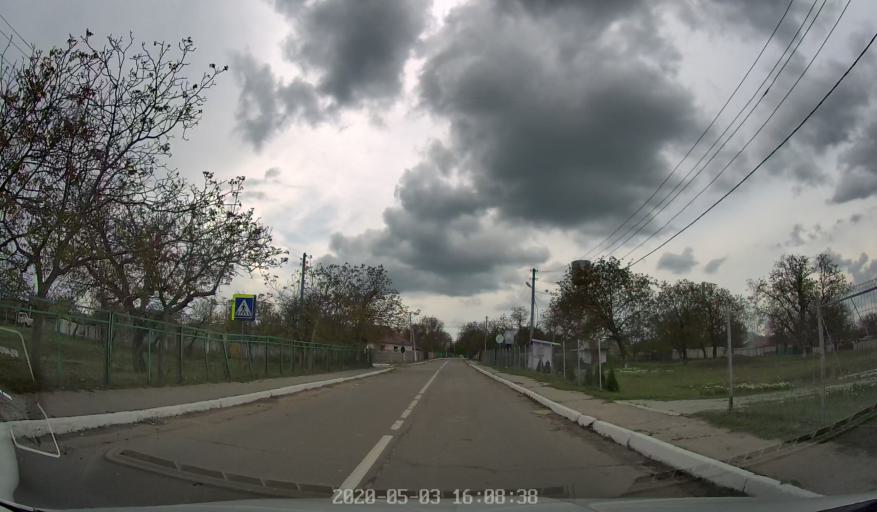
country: MD
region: Calarasi
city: Calarasi
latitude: 47.1966
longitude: 28.3446
